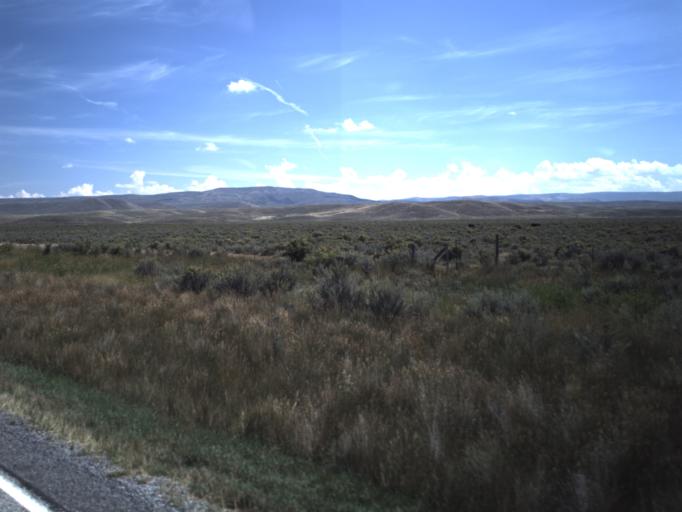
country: US
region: Utah
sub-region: Rich County
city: Randolph
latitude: 41.7777
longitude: -111.0668
